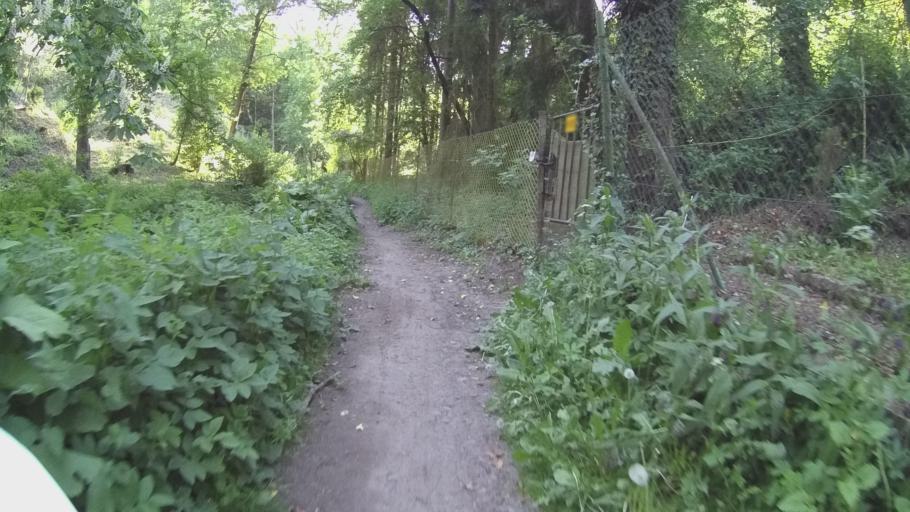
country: CZ
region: Central Bohemia
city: Roztoky
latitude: 50.1482
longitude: 14.4126
